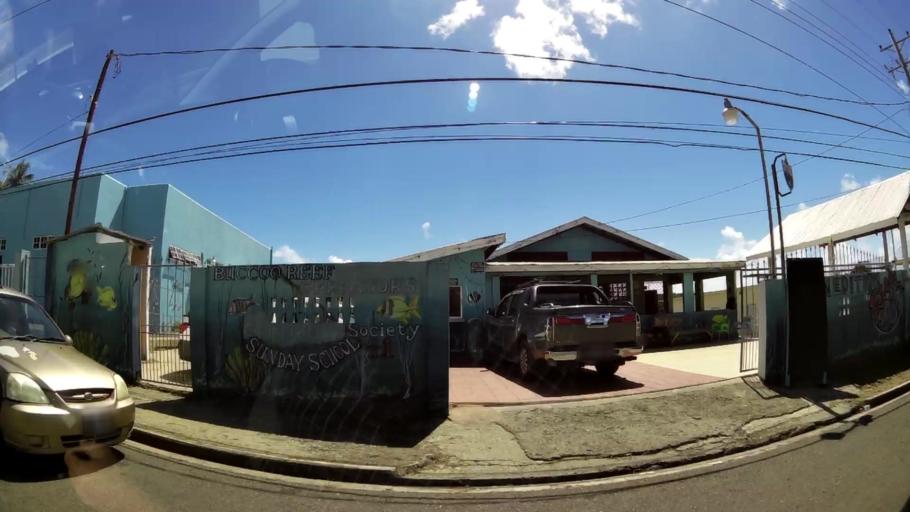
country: TT
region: Tobago
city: Scarborough
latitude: 11.1819
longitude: -60.8058
